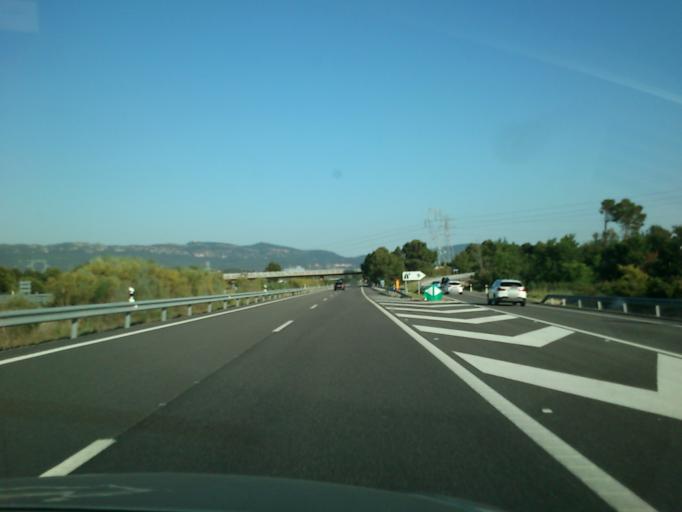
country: ES
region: Catalonia
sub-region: Provincia de Tarragona
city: Montblanc
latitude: 41.3950
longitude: 1.1621
